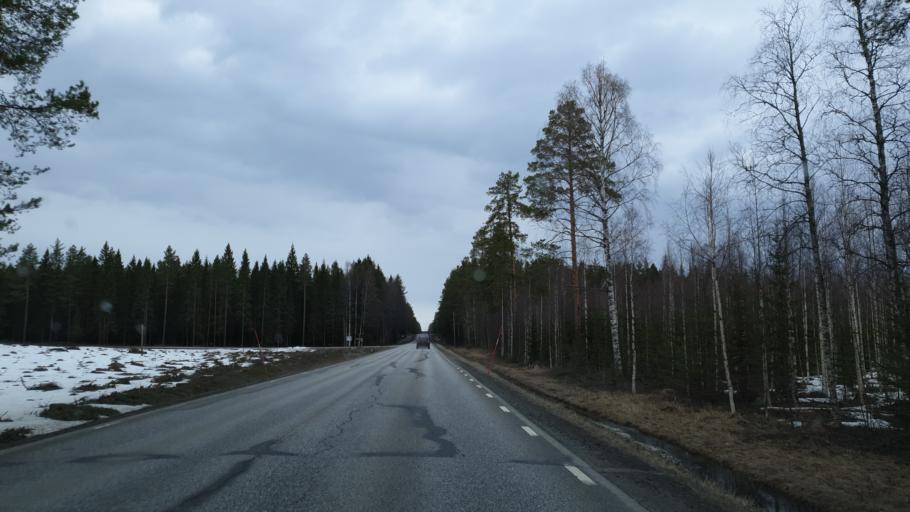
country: SE
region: Vaesterbotten
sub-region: Skelleftea Kommun
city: Viken
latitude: 64.6523
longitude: 20.9551
